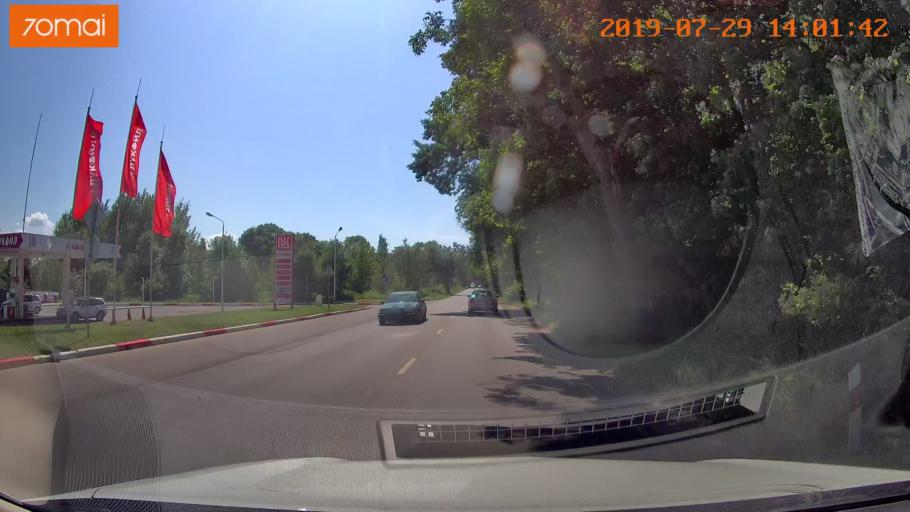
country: RU
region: Kaliningrad
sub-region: Gorod Kaliningrad
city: Baltiysk
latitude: 54.6684
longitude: 19.9198
